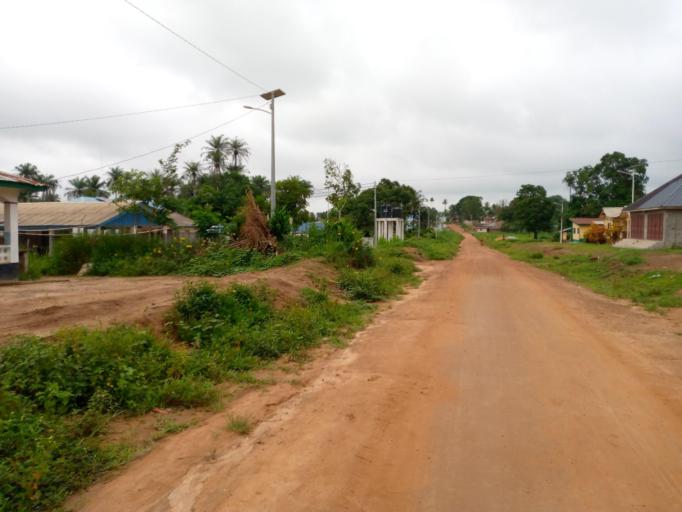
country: SL
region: Southern Province
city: Sumbuya
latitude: 7.5668
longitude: -12.0900
